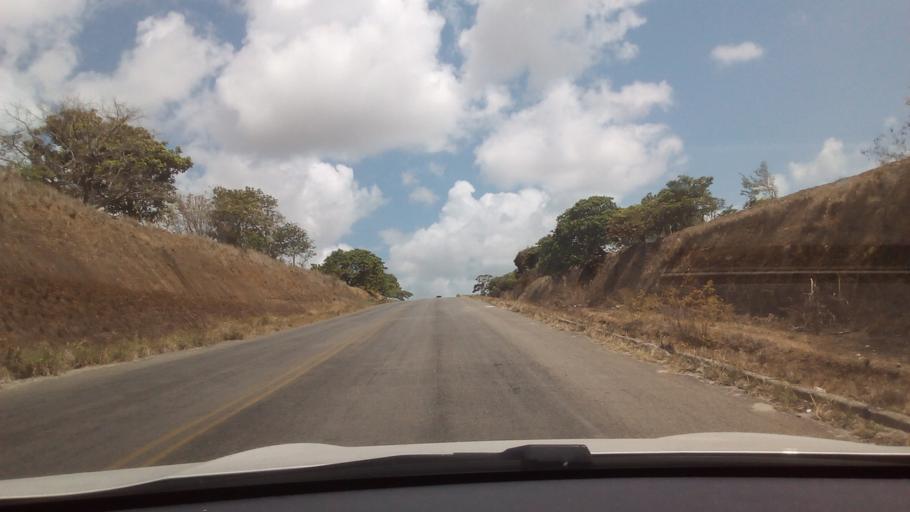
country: BR
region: Paraiba
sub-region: Conde
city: Conde
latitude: -7.2262
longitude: -34.8407
